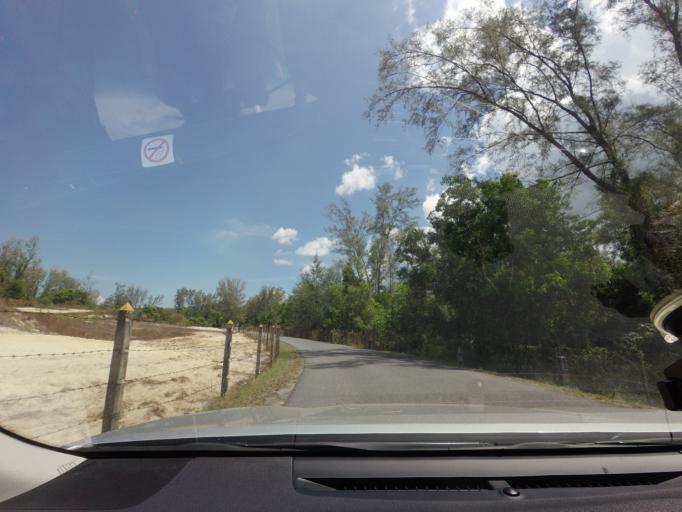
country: TH
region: Phuket
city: Thalang
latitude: 8.0328
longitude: 98.2905
